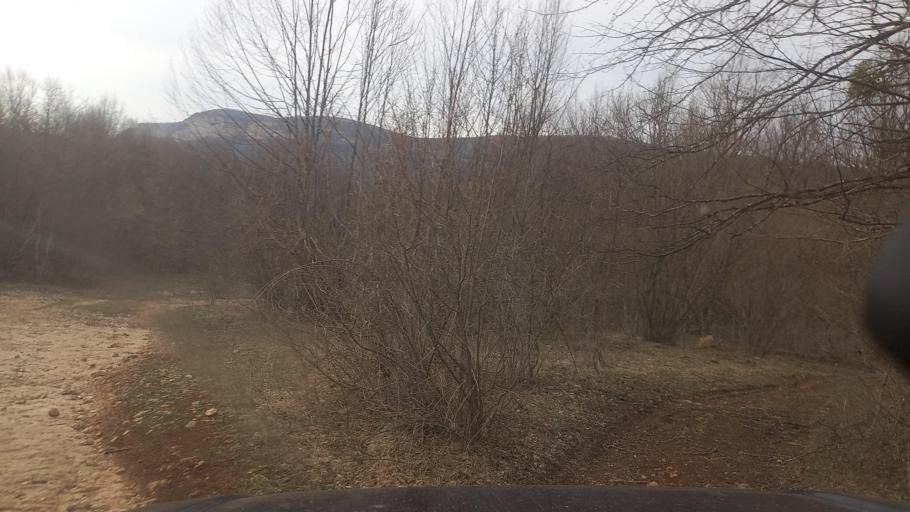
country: RU
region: Adygeya
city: Kamennomostskiy
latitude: 44.1904
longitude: 39.9671
